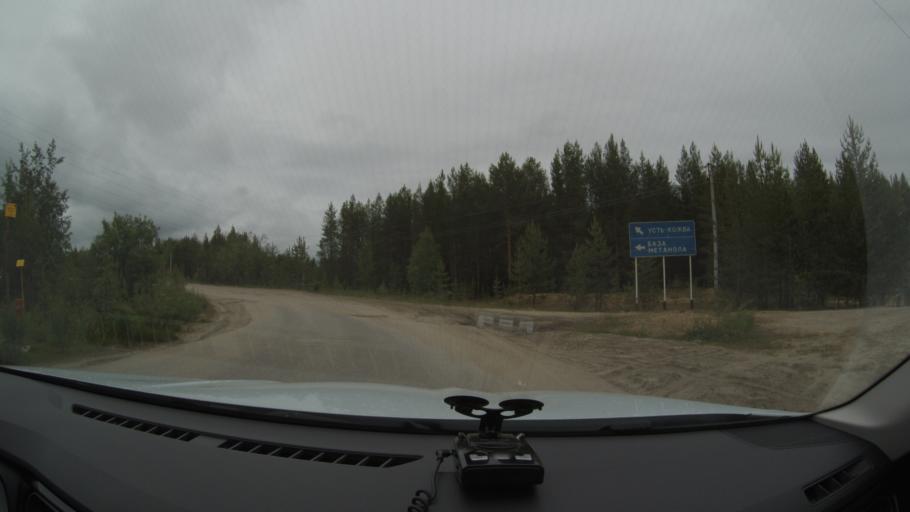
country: RU
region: Komi Republic
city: Kozhva
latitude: 65.1122
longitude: 57.0034
